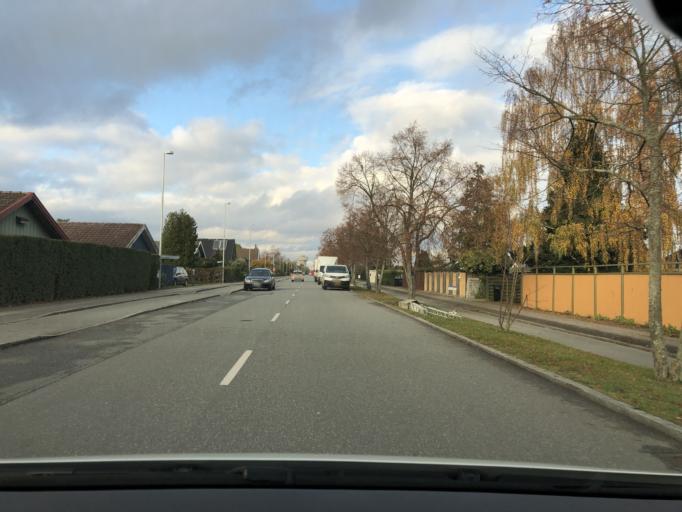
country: DK
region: Capital Region
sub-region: Tarnby Kommune
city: Tarnby
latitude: 55.6117
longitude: 12.5933
